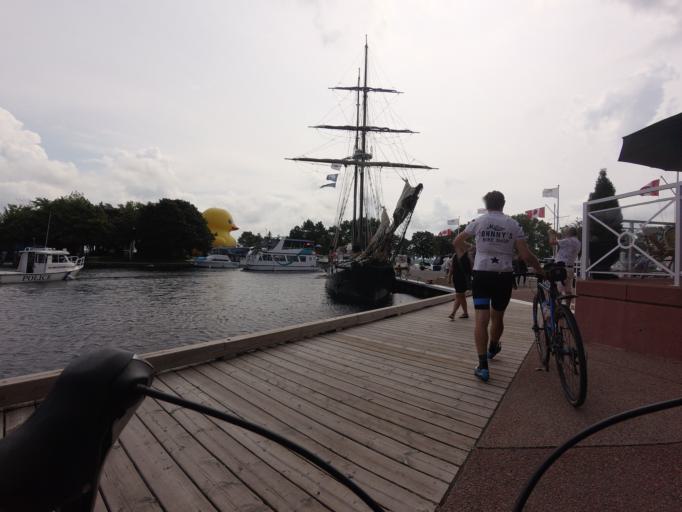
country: CA
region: Ontario
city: Brockville
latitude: 44.5877
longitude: -75.6821
